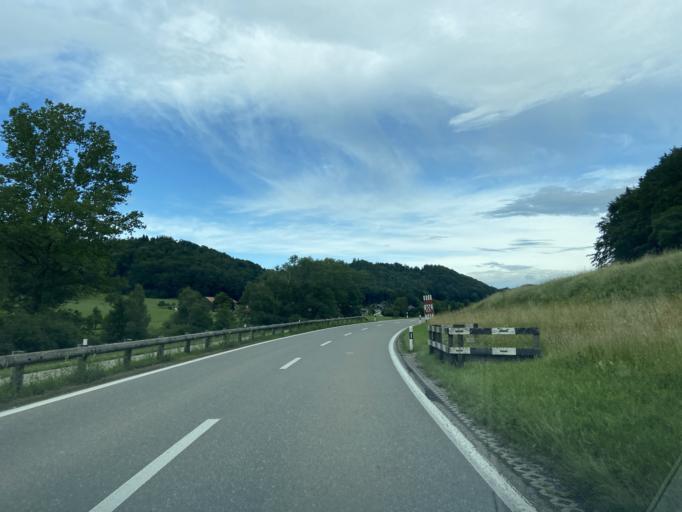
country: CH
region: Thurgau
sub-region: Muenchwilen District
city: Aadorf
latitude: 47.4564
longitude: 8.9021
